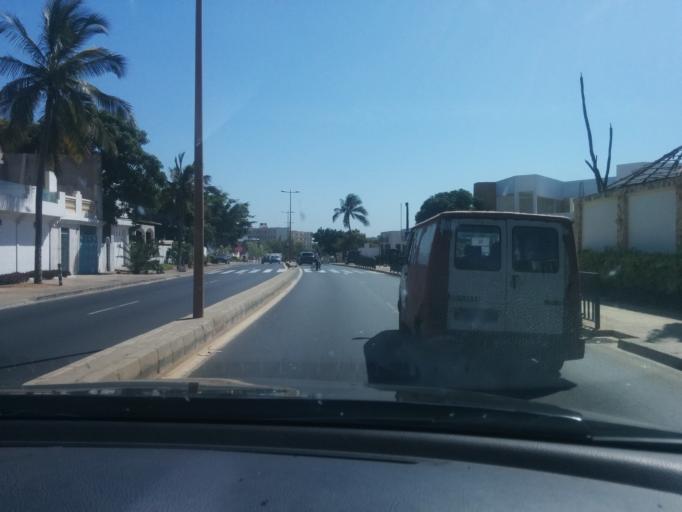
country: SN
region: Dakar
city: Mermoz Boabab
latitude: 14.7084
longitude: -17.4858
